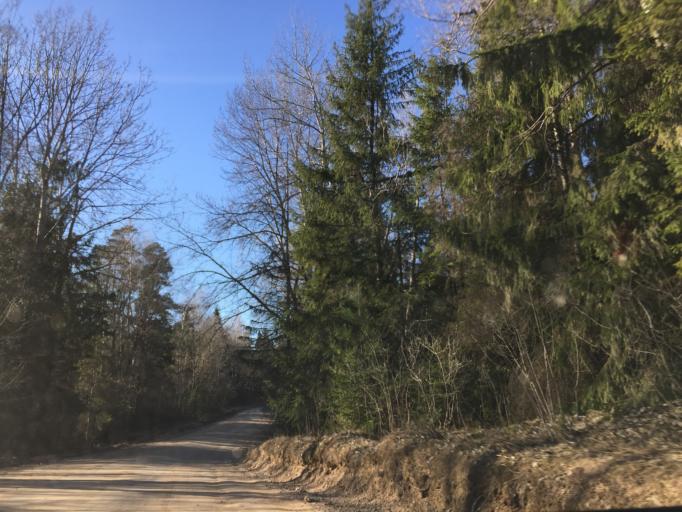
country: LV
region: Ropazu
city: Ropazi
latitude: 56.9178
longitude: 24.7136
